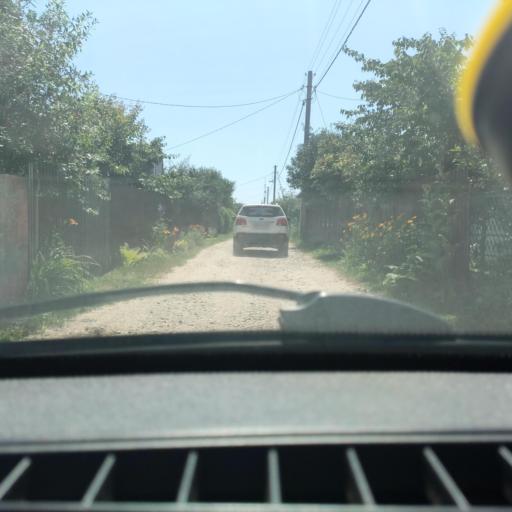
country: RU
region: Samara
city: Tol'yatti
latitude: 53.5937
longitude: 49.3052
